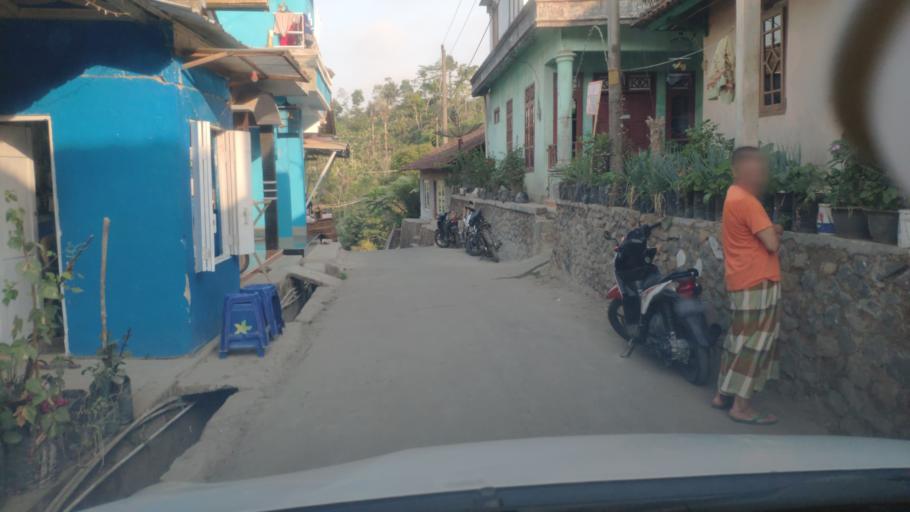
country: ID
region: Central Java
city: Wonosobo
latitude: -7.4350
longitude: 109.7588
